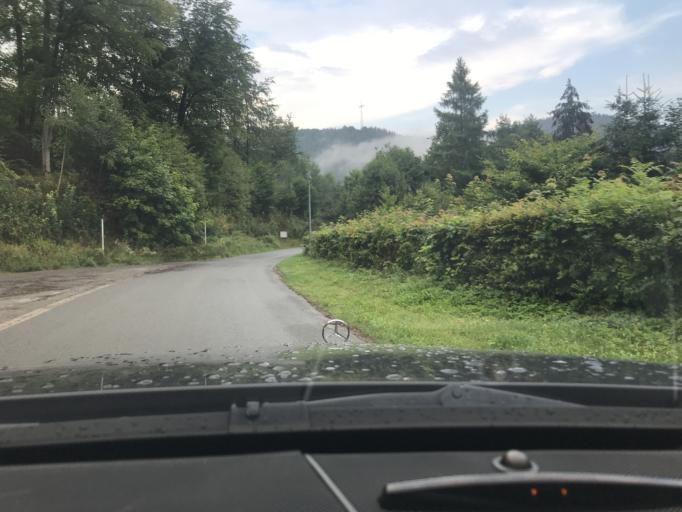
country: DE
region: Lower Saxony
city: Bad Lauterberg im Harz
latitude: 51.6453
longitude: 10.5134
